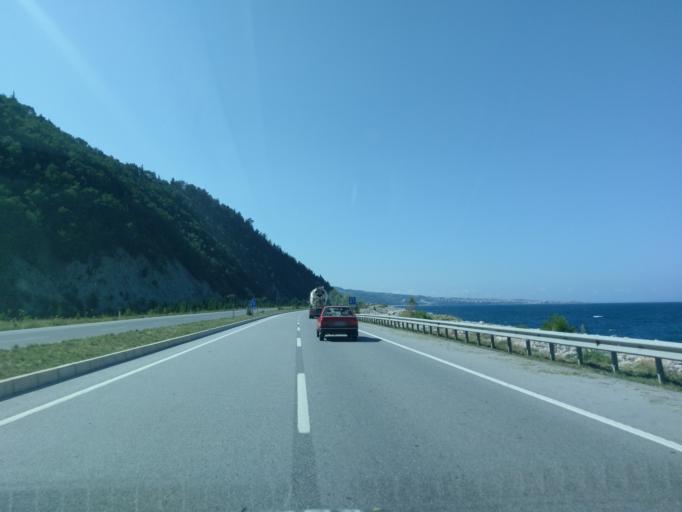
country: TR
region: Sinop
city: Gerze
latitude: 41.7468
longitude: 35.2447
